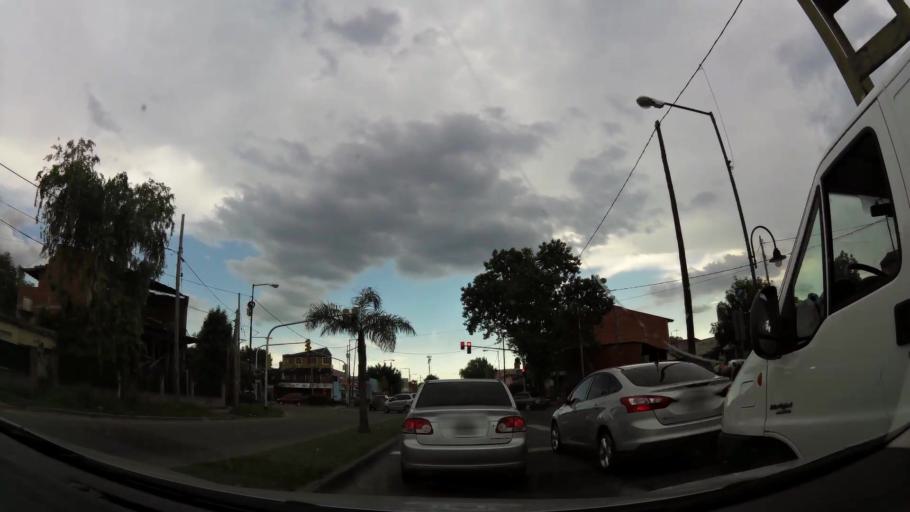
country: AR
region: Buenos Aires
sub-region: Partido de Tigre
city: Tigre
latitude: -34.4779
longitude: -58.5800
